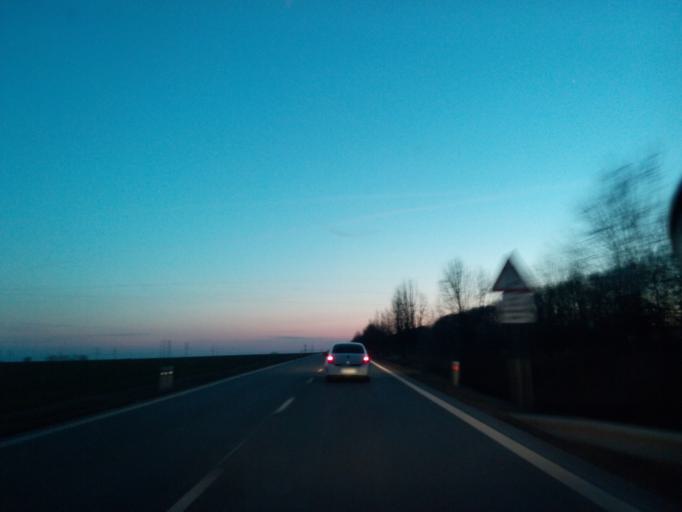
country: SK
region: Kosicky
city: Michalovce
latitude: 48.7200
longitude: 21.8479
